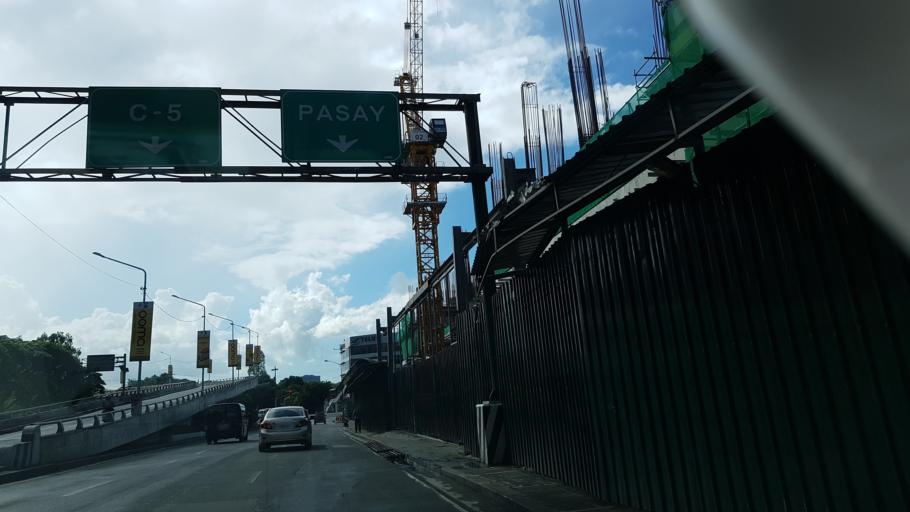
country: PH
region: Metro Manila
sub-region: Makati City
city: Makati City
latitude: 14.5516
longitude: 121.0282
